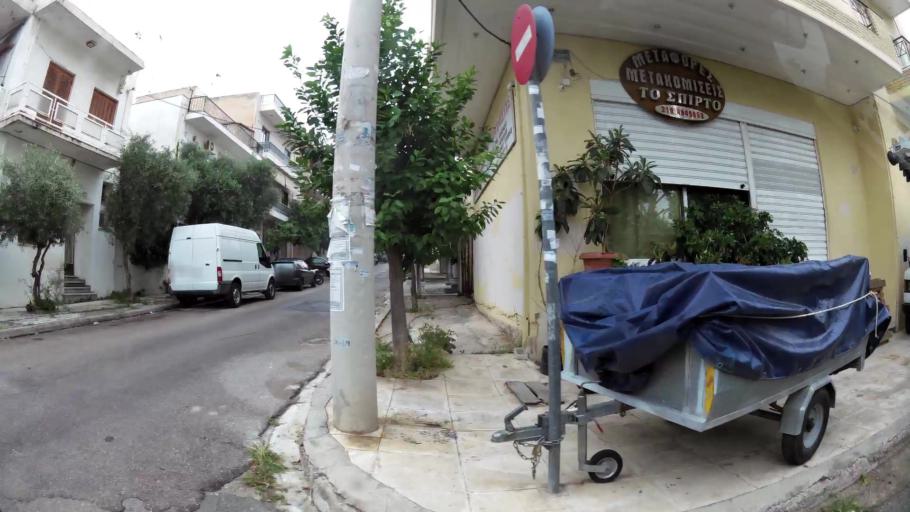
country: GR
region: Attica
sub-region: Nomos Piraios
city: Korydallos
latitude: 37.9836
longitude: 23.6531
